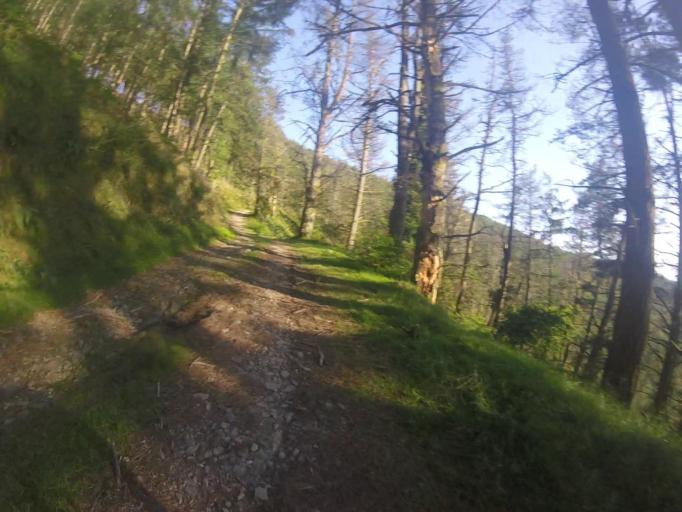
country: ES
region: Navarre
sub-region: Provincia de Navarra
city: Arano
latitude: 43.2459
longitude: -1.8519
